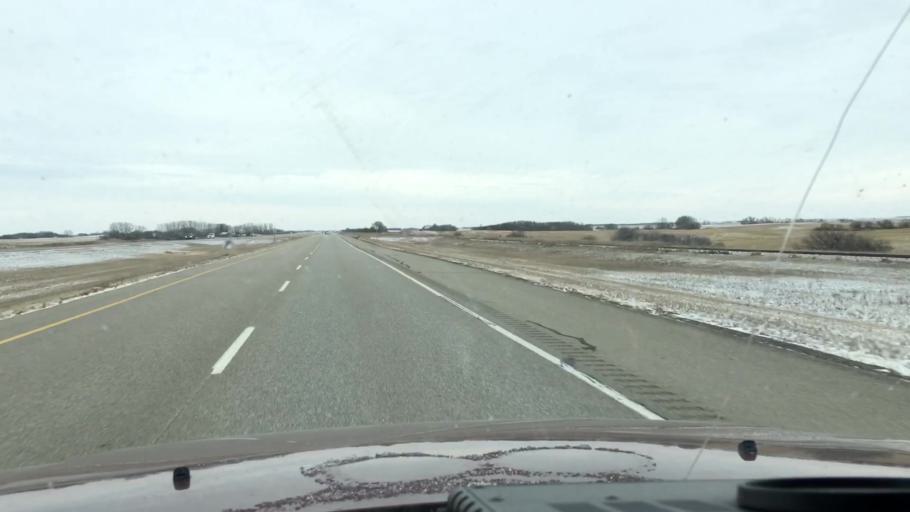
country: CA
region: Saskatchewan
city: Watrous
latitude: 51.3488
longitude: -106.1140
